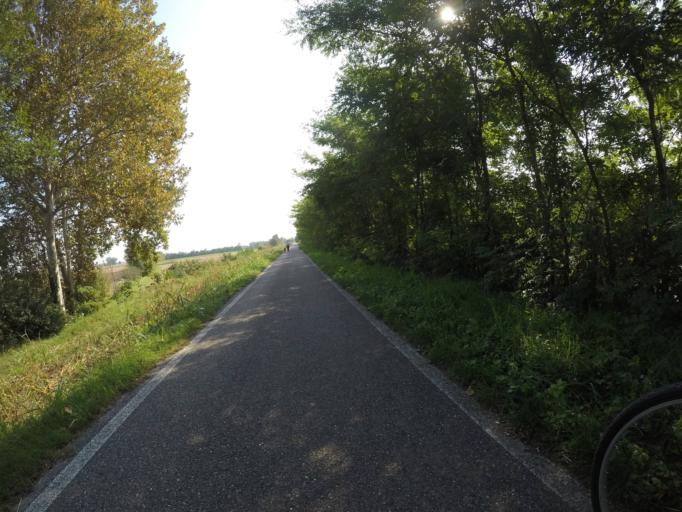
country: IT
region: Veneto
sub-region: Provincia di Rovigo
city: Frassinelle Polesine
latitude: 44.9966
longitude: 11.7025
